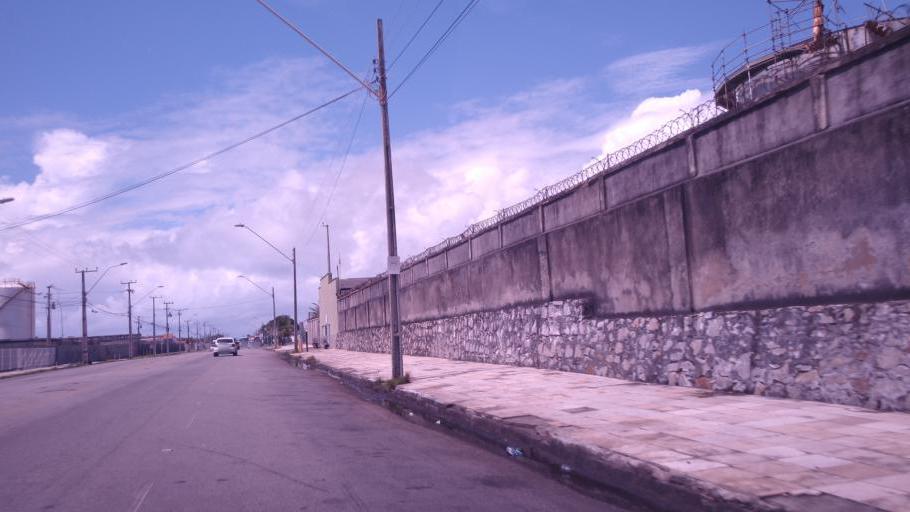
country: BR
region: Ceara
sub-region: Fortaleza
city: Fortaleza
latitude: -3.7152
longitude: -38.4704
